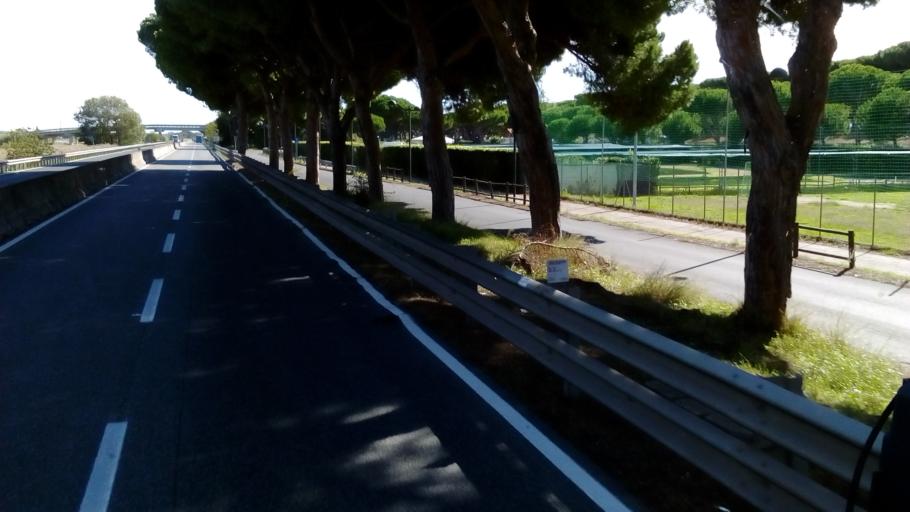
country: IT
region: Tuscany
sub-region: Provincia di Grosseto
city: Albinia
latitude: 42.5264
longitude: 11.1894
